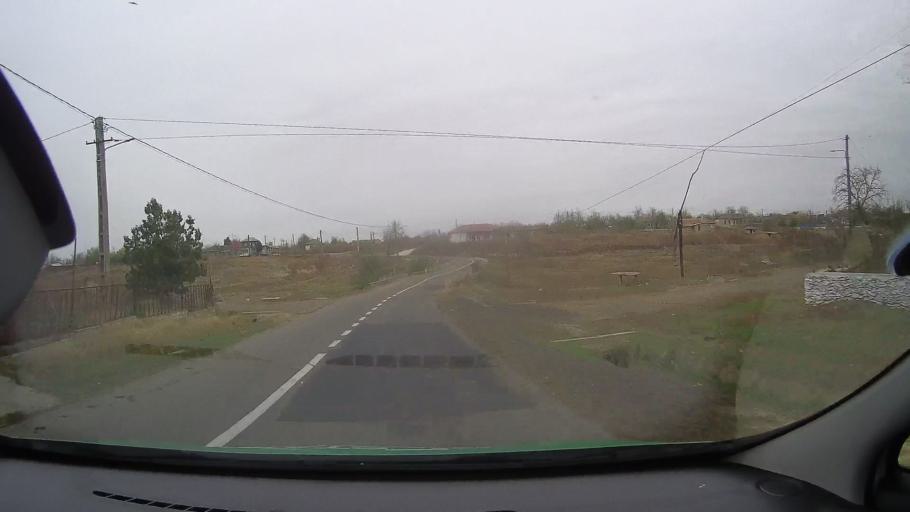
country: RO
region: Constanta
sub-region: Comuna Vulturu
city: Vulturu
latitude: 44.7000
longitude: 28.2405
